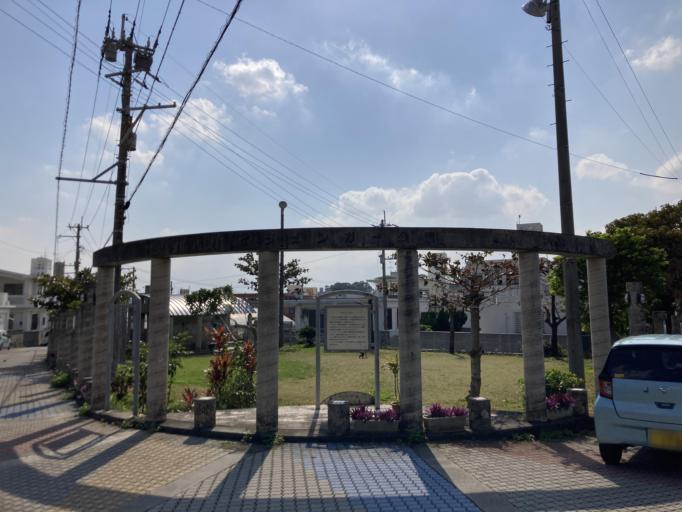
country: JP
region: Okinawa
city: Tomigusuku
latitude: 26.1900
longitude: 127.7271
